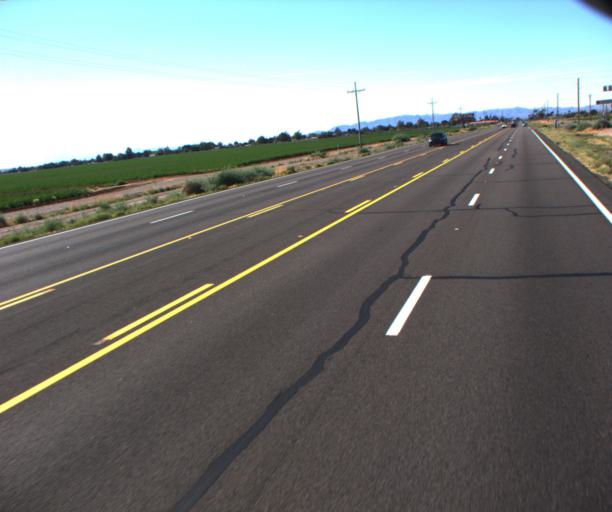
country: US
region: Arizona
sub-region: Mohave County
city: Willow Valley
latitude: 34.9208
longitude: -114.5979
